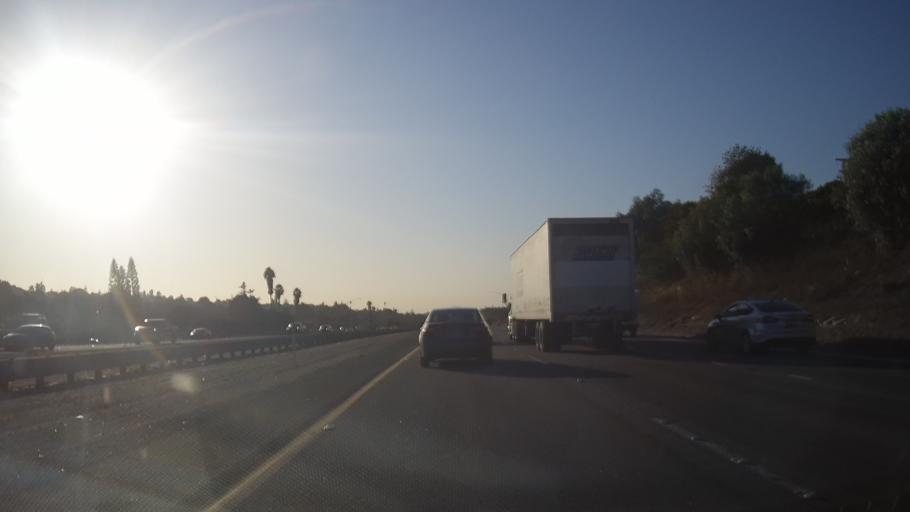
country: US
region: California
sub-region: San Diego County
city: Casa de Oro-Mount Helix
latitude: 32.7447
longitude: -116.9677
